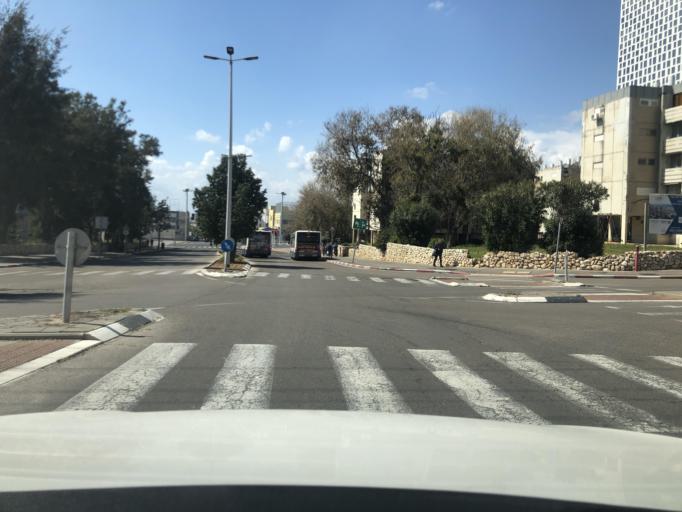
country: IL
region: Tel Aviv
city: Bat Yam
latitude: 32.0108
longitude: 34.7532
